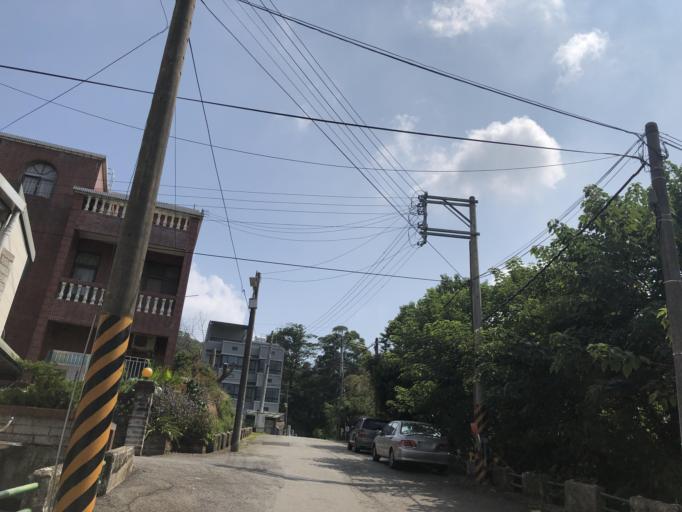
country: TW
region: Taiwan
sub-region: Miaoli
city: Miaoli
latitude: 24.4731
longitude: 120.7937
